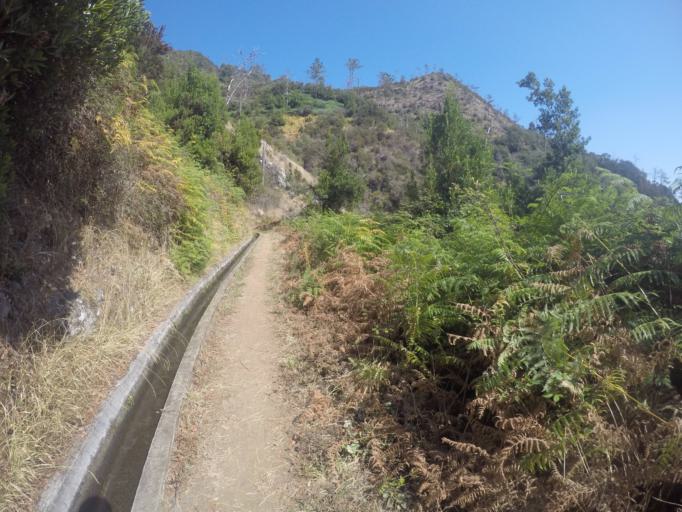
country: PT
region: Madeira
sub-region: Santana
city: Santana
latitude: 32.7547
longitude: -16.8379
